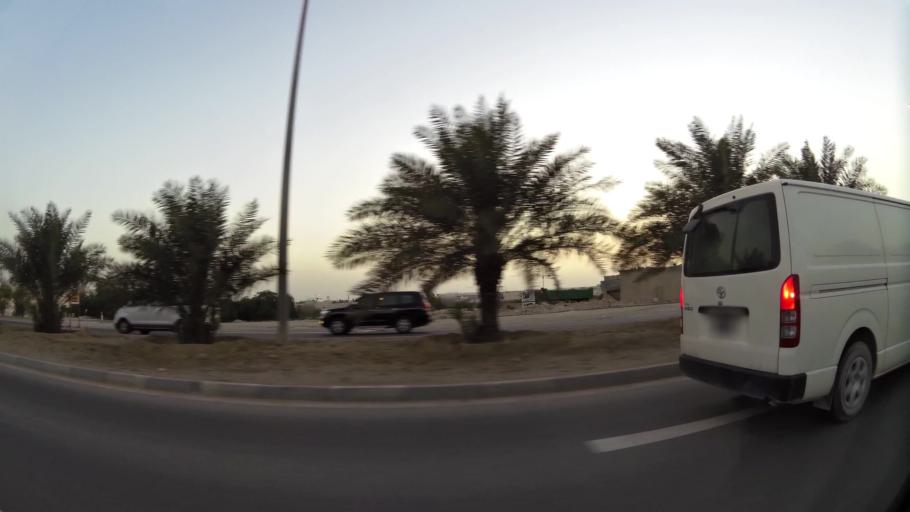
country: QA
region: Baladiyat ar Rayyan
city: Ar Rayyan
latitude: 25.3116
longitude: 51.4611
